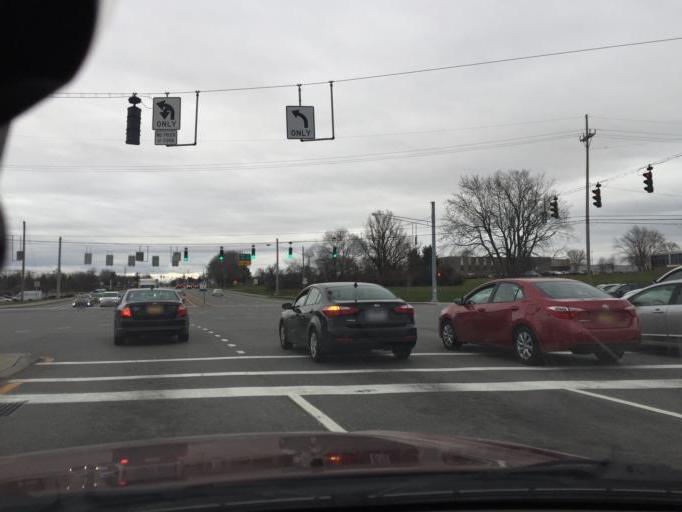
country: US
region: New York
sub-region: Monroe County
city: Rochester
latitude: 43.0876
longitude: -77.6093
